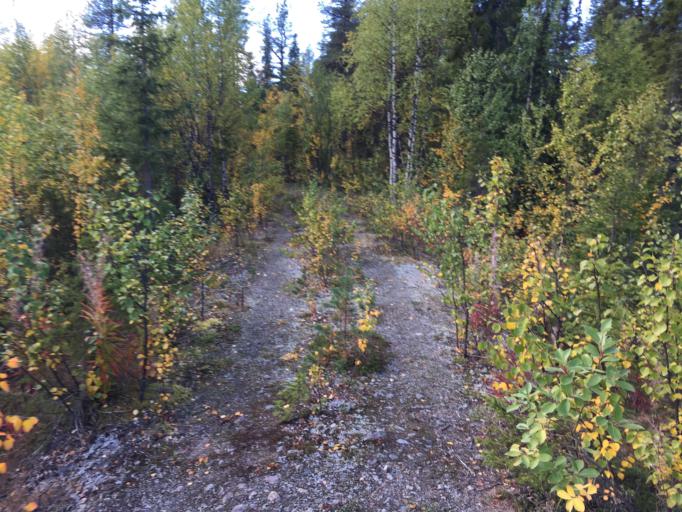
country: SE
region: Norrbotten
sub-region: Gallivare Kommun
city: Malmberget
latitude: 67.6309
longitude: 20.9382
